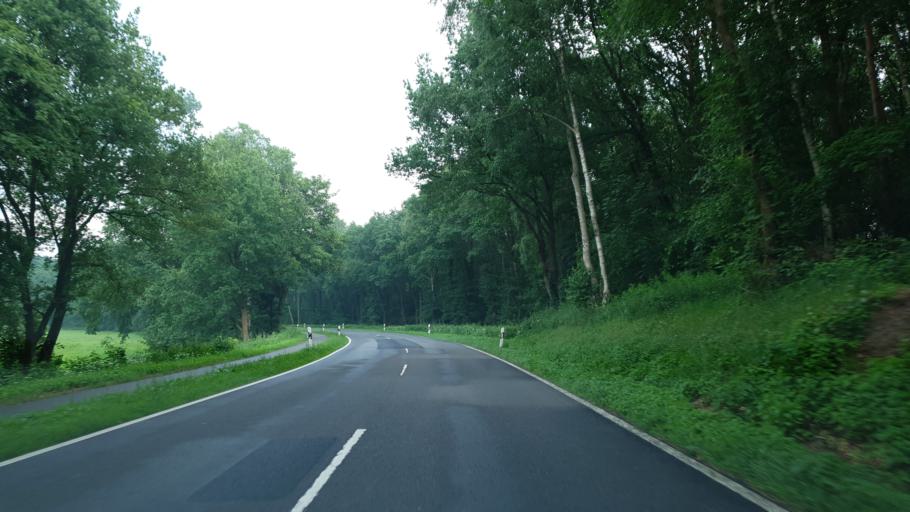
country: DE
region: Lower Saxony
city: Meppen
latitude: 52.6805
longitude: 7.3275
